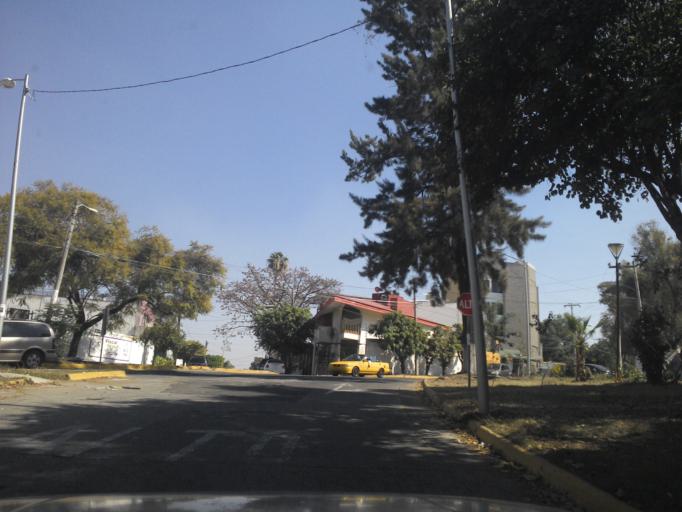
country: MX
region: Jalisco
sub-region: Zapopan
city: Zapopan
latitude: 20.7065
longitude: -103.3601
